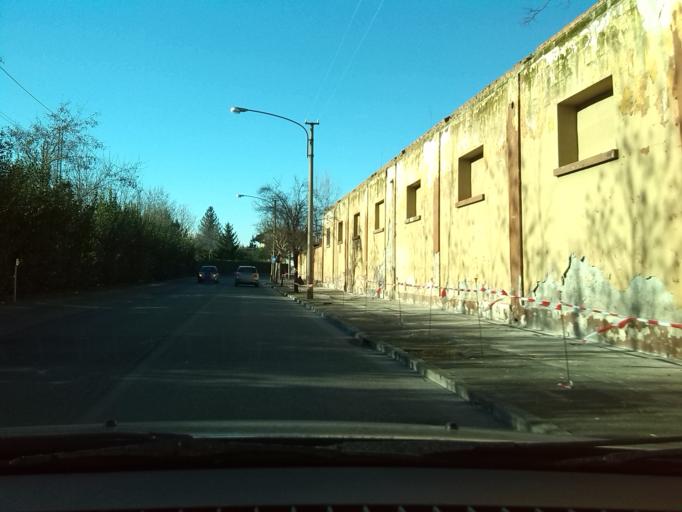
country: IT
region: Friuli Venezia Giulia
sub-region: Provincia di Gorizia
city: Cormons
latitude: 45.9540
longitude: 13.4691
